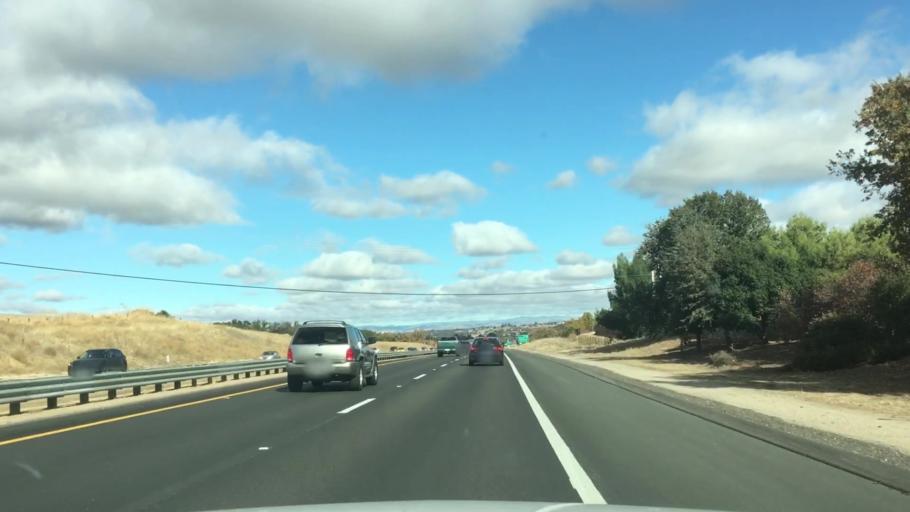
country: US
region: California
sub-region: San Luis Obispo County
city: Templeton
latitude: 35.5578
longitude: -120.7095
